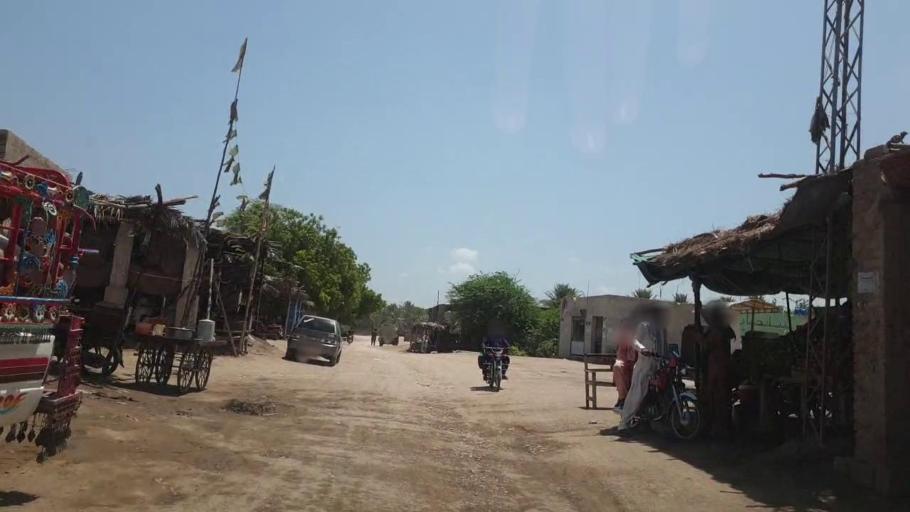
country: PK
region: Sindh
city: Pano Aqil
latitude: 27.6623
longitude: 69.1645
